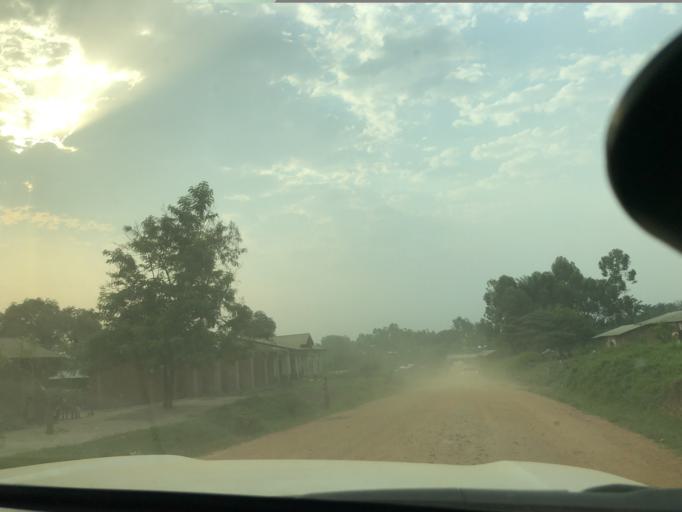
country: UG
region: Western Region
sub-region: Kasese District
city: Margherita
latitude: 0.3411
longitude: 29.6684
